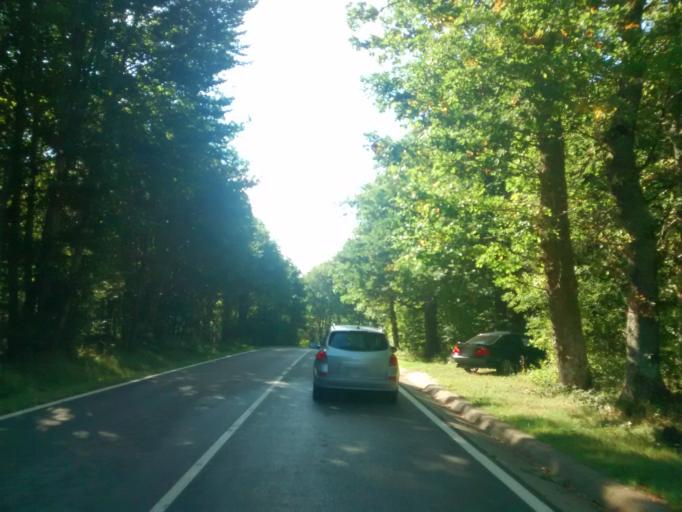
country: ES
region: Cantabria
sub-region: Provincia de Cantabria
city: Reinosa
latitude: 42.9561
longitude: -4.0553
